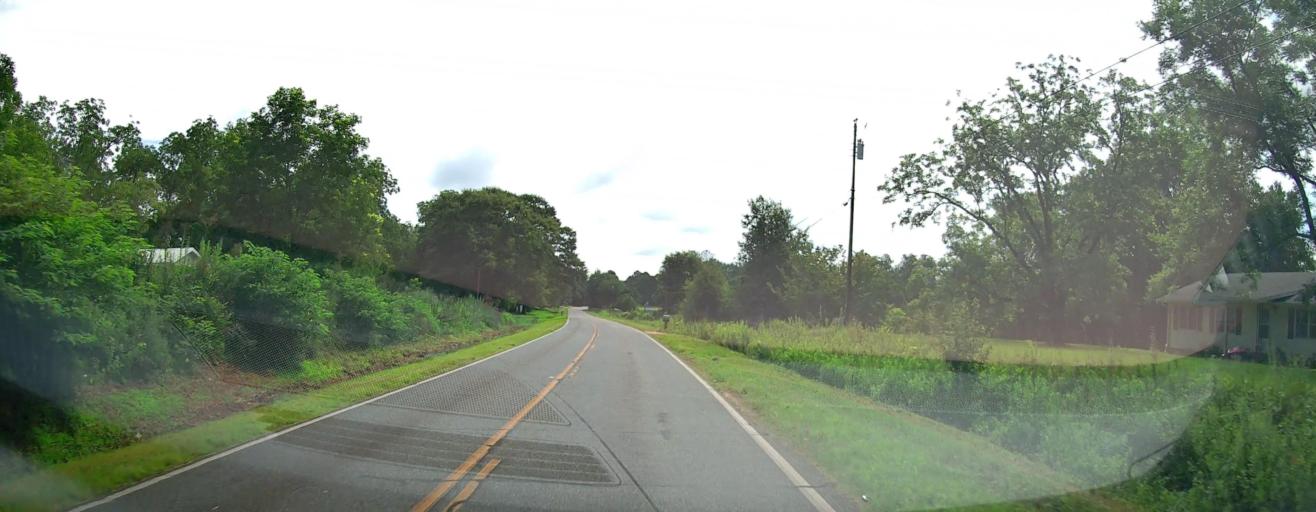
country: US
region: Georgia
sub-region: Peach County
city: Byron
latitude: 32.6430
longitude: -83.7907
